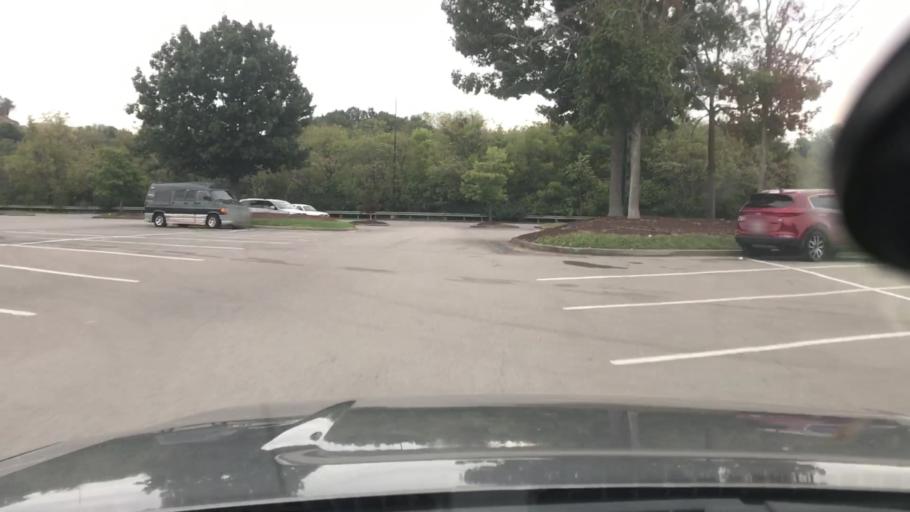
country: US
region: Tennessee
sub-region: Davidson County
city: Belle Meade
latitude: 36.1311
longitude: -86.9062
